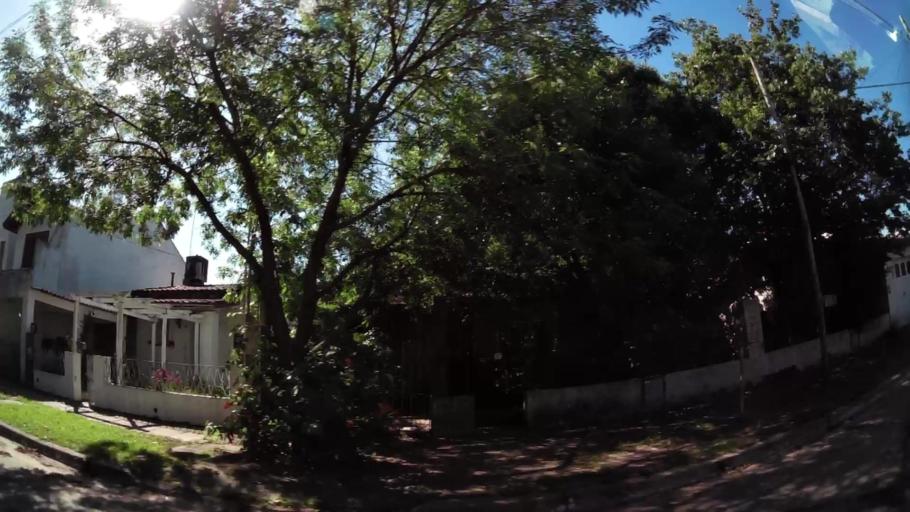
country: AR
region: Buenos Aires
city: Hurlingham
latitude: -34.4980
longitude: -58.6884
